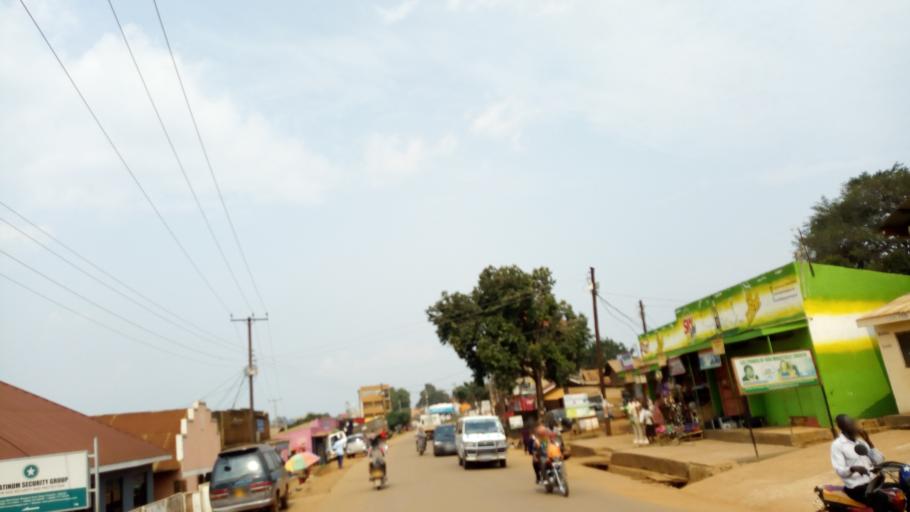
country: UG
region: Central Region
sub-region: Wakiso District
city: Kireka
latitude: 0.3216
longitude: 32.6441
